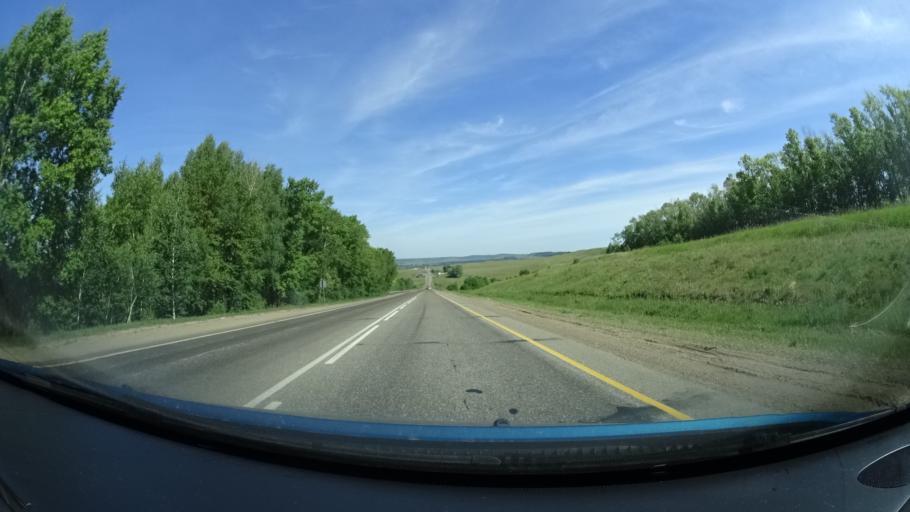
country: RU
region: Bashkortostan
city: Blagoveshchensk
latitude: 55.1600
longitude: 55.8531
